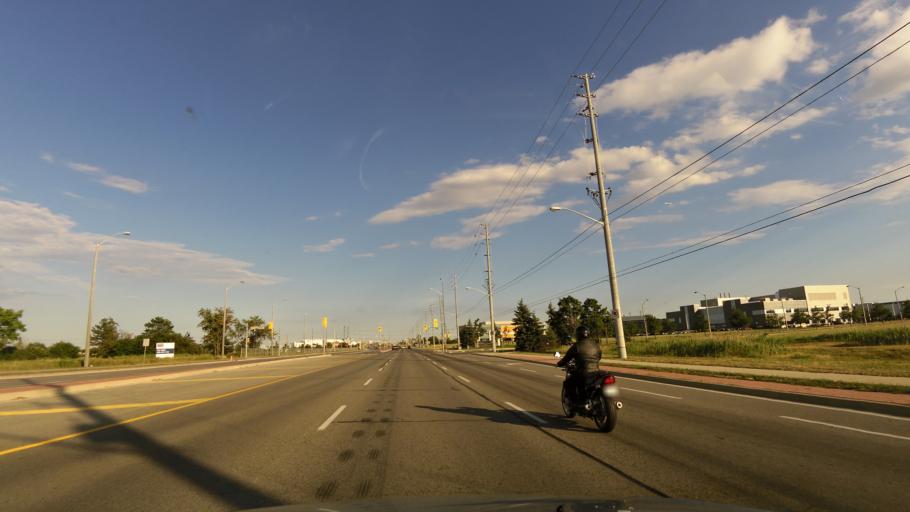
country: CA
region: Ontario
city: Brampton
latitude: 43.6241
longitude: -79.7717
